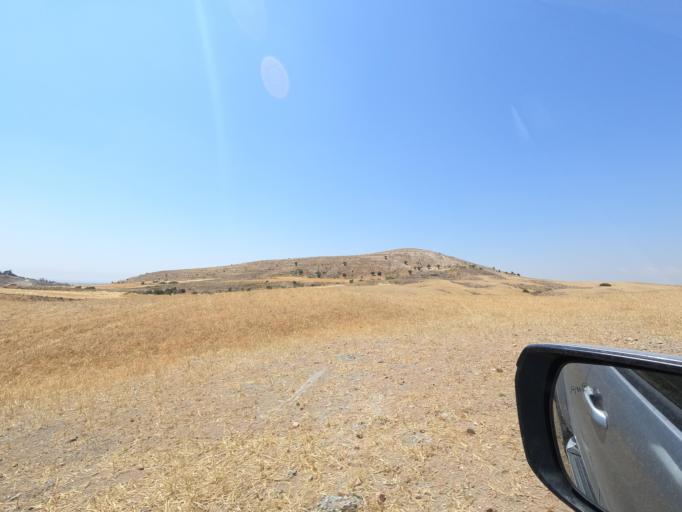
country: CY
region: Larnaka
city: Troulloi
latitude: 34.9993
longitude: 33.6177
